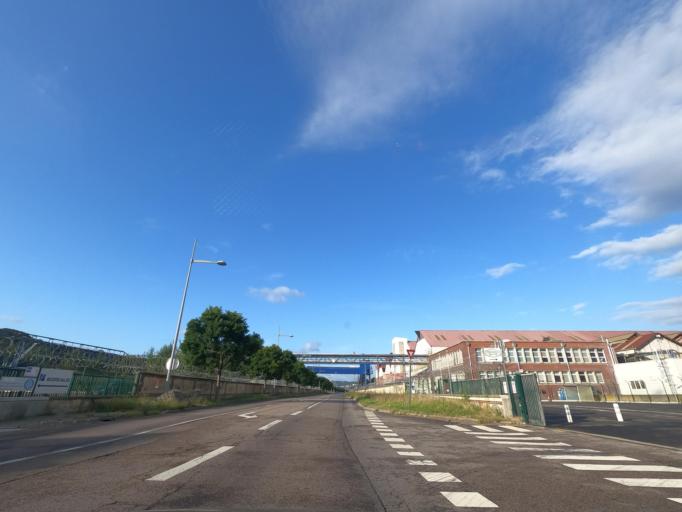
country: FR
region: Haute-Normandie
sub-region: Departement de la Seine-Maritime
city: Canteleu
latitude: 49.4211
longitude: 1.0253
